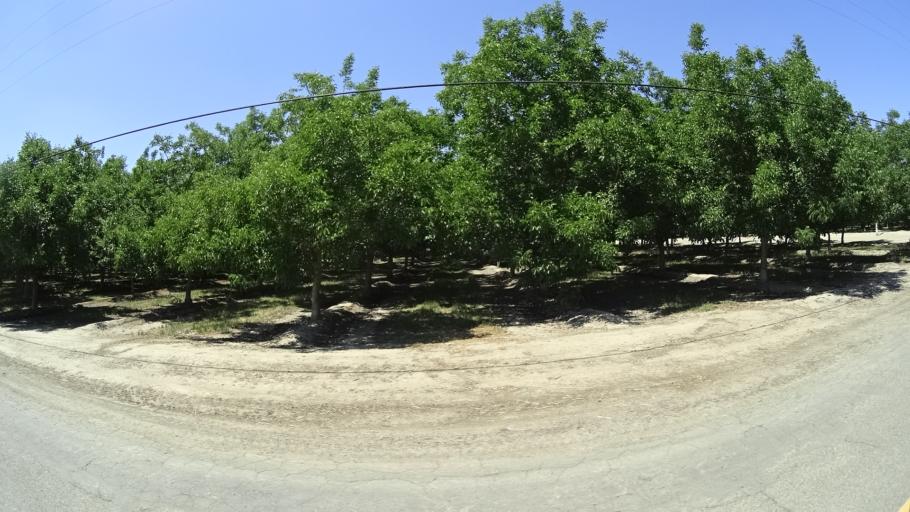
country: US
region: California
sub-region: Kings County
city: Lucerne
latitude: 36.4115
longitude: -119.6189
